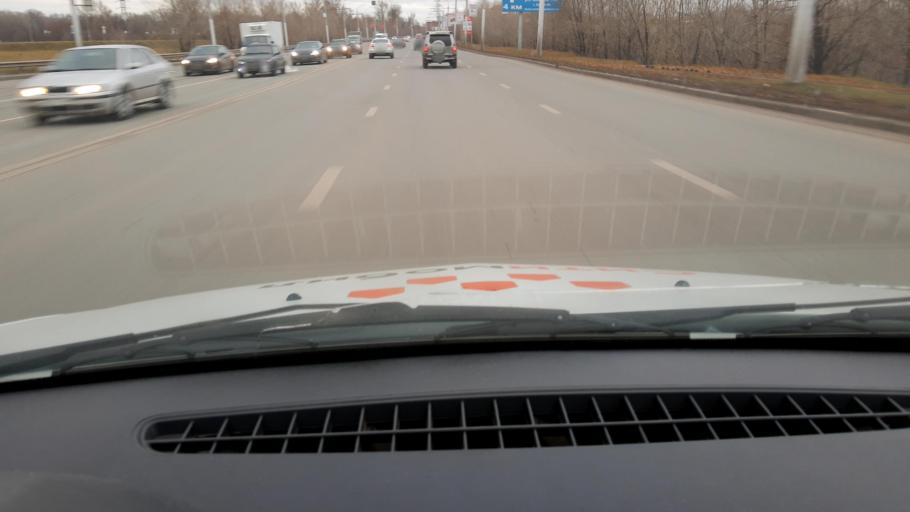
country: RU
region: Bashkortostan
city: Ufa
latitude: 54.7920
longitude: 56.0774
